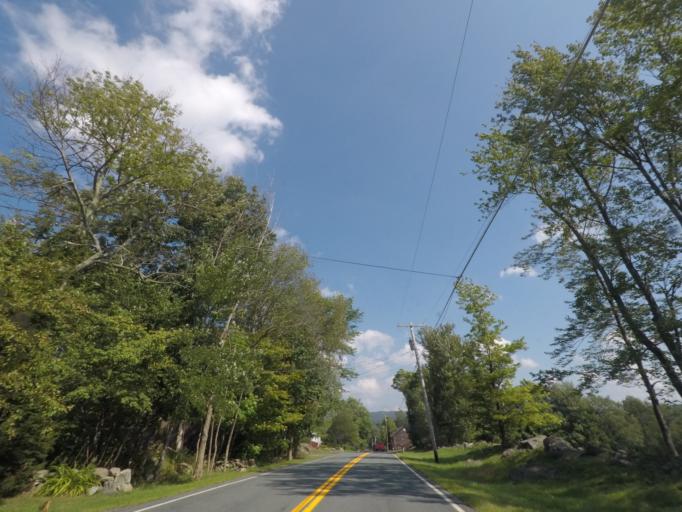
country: US
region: New York
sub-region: Rensselaer County
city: Poestenkill
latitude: 42.6826
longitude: -73.5212
